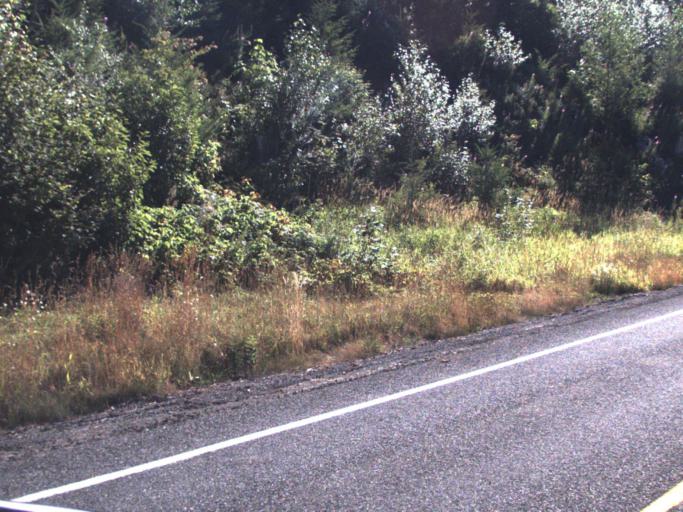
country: US
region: Washington
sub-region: King County
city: Enumclaw
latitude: 47.1564
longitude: -121.8635
